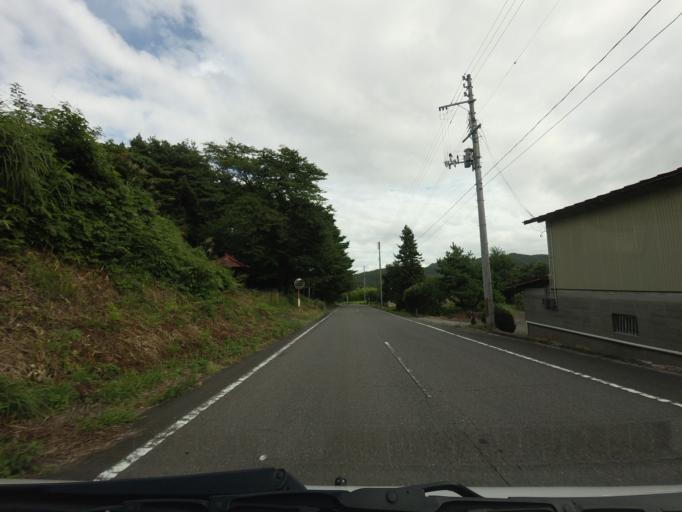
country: JP
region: Fukushima
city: Motomiya
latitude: 37.5405
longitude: 140.3336
